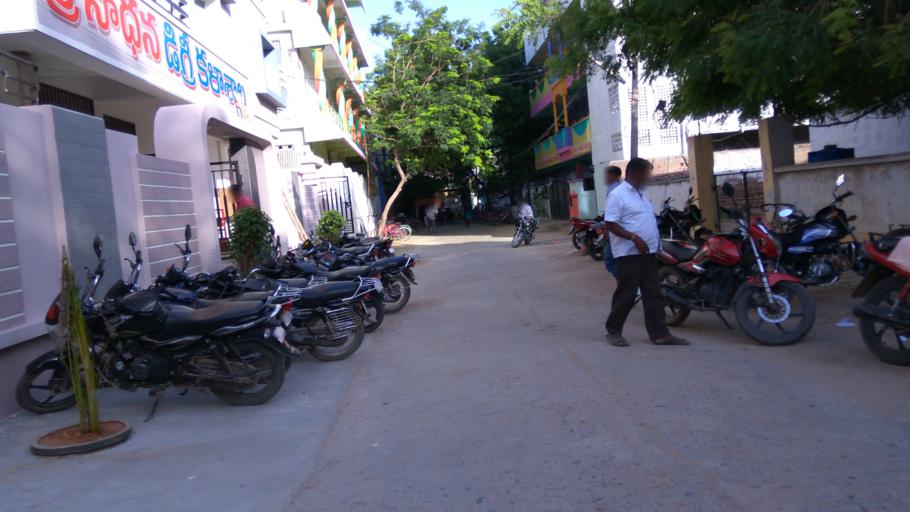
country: IN
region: Andhra Pradesh
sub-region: Prakasam
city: Markapur
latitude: 15.7437
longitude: 79.2731
